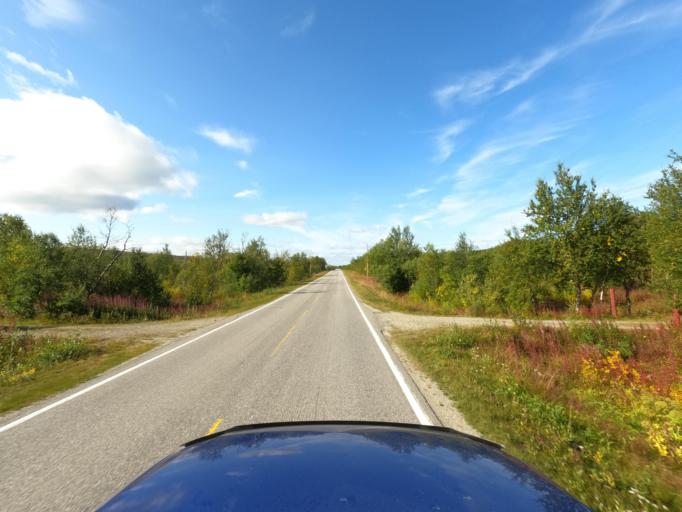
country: NO
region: Finnmark Fylke
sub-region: Porsanger
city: Lakselv
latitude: 69.7633
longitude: 25.1958
